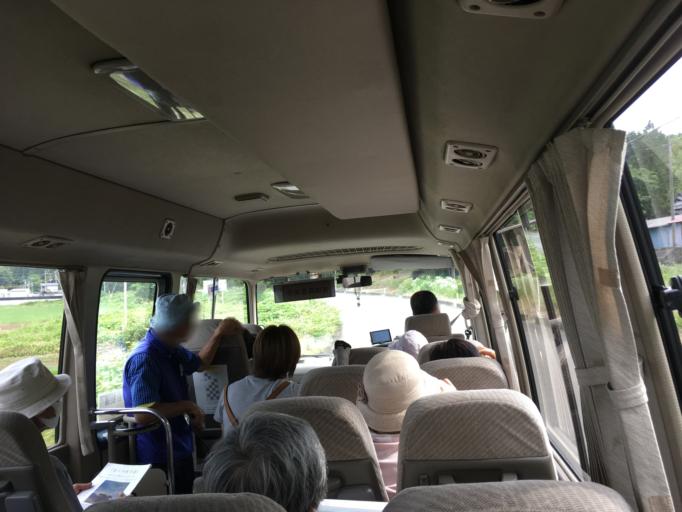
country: JP
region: Iwate
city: Ichinoseki
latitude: 38.7358
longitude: 141.2558
